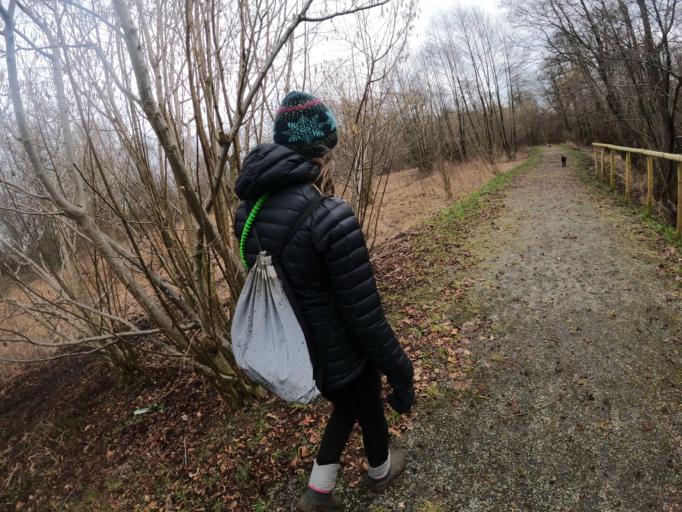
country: PL
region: West Pomeranian Voivodeship
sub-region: Powiat kolobrzeski
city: Goscino
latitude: 54.0409
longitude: 15.6679
